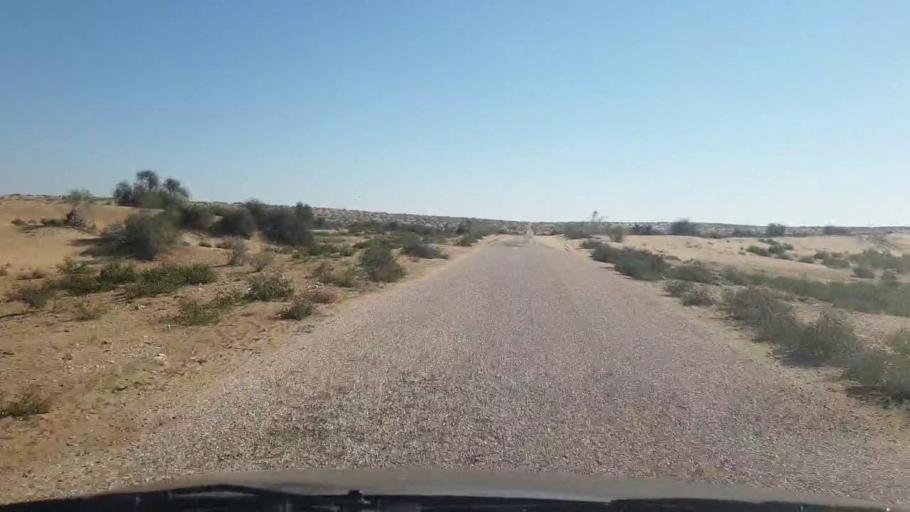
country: PK
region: Sindh
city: Bozdar
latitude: 27.0101
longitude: 68.7977
